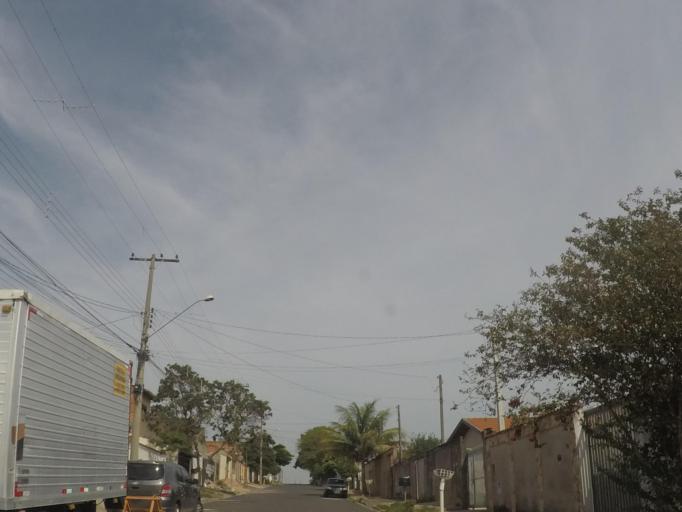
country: BR
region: Sao Paulo
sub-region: Hortolandia
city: Hortolandia
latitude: -22.8474
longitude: -47.1961
